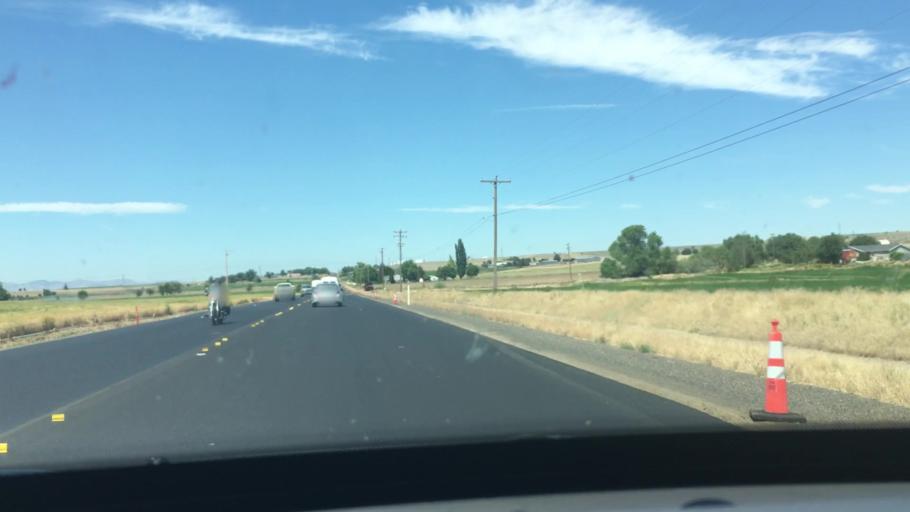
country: US
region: Oregon
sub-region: Jefferson County
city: Culver
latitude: 44.5509
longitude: -121.1686
